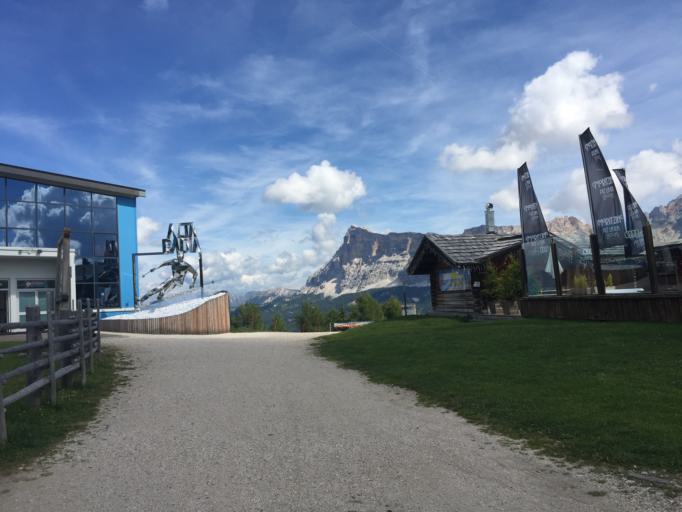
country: IT
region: Trentino-Alto Adige
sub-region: Bolzano
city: Corvara in Badia
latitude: 46.5652
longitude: 11.9062
